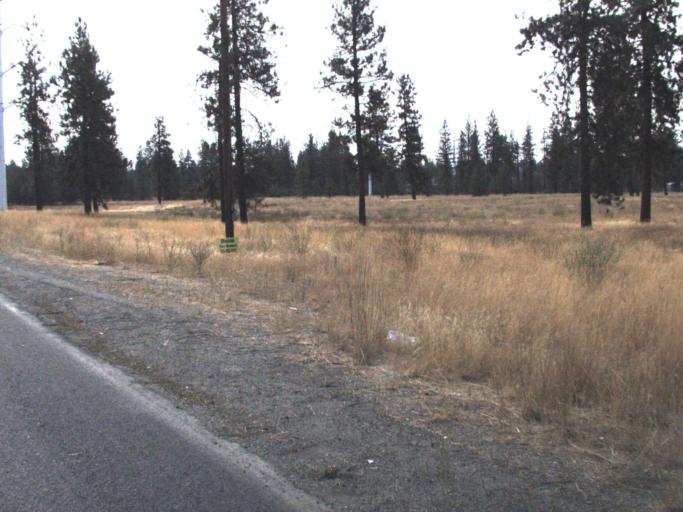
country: US
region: Washington
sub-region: Spokane County
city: Town and Country
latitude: 47.7327
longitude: -117.5048
